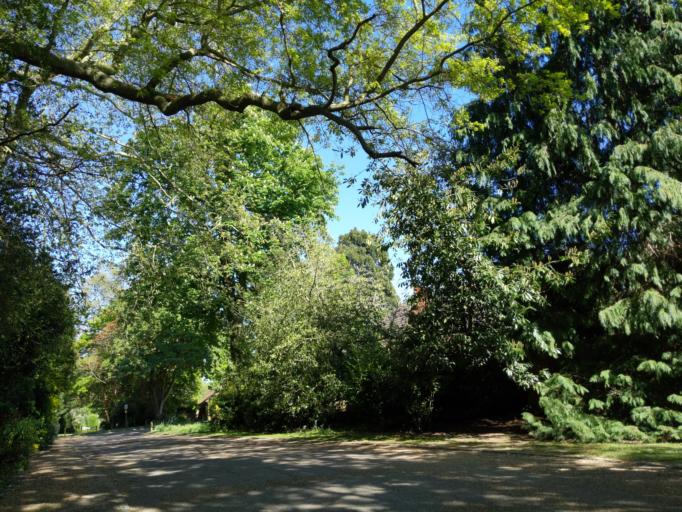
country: GB
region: England
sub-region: Surrey
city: Esher
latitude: 51.3700
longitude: -0.3563
